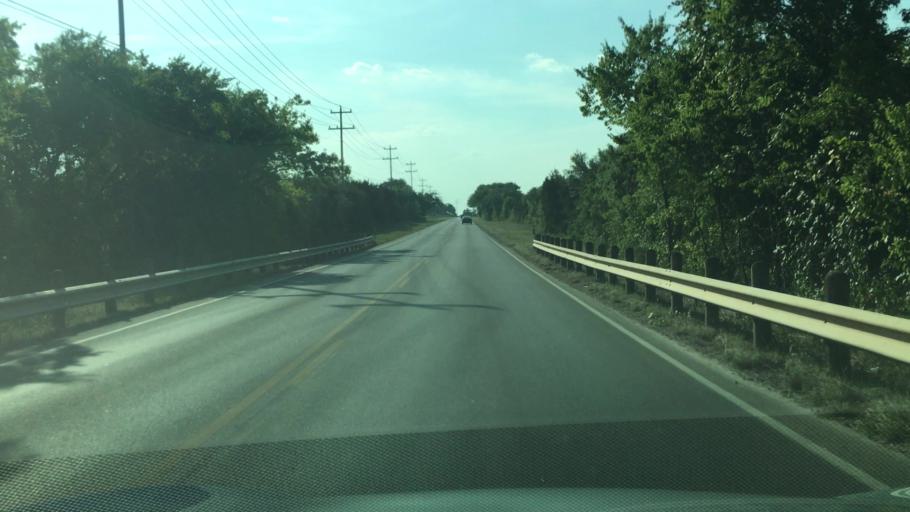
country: US
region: Texas
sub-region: Hays County
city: Buda
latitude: 30.0976
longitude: -97.9321
